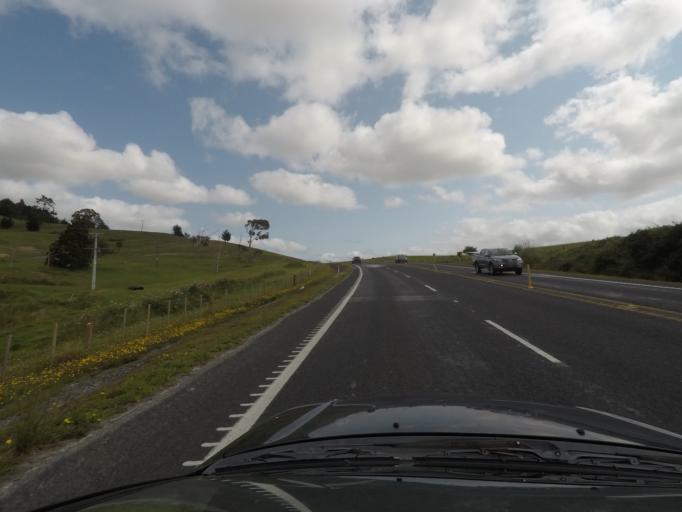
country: NZ
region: Northland
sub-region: Whangarei
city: Whangarei
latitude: -35.8115
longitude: 174.2972
